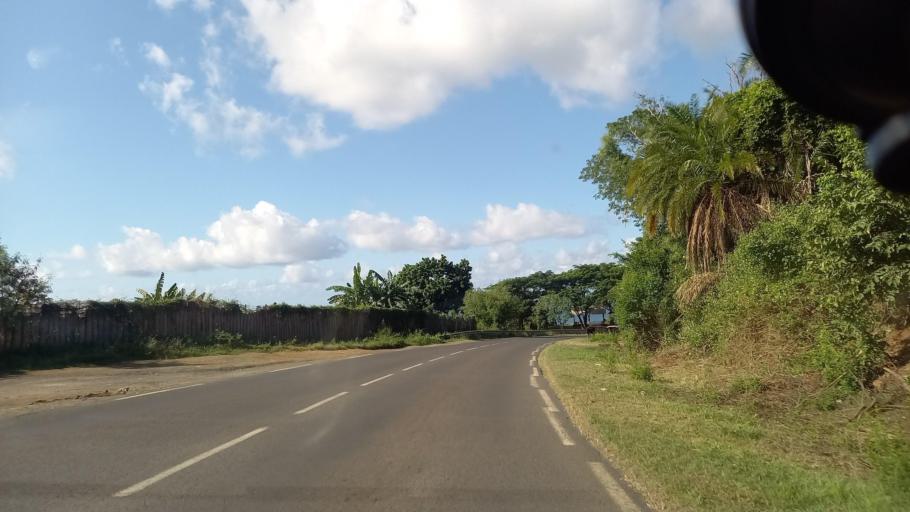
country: YT
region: Koungou
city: Koungou
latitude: -12.7314
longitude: 45.1969
